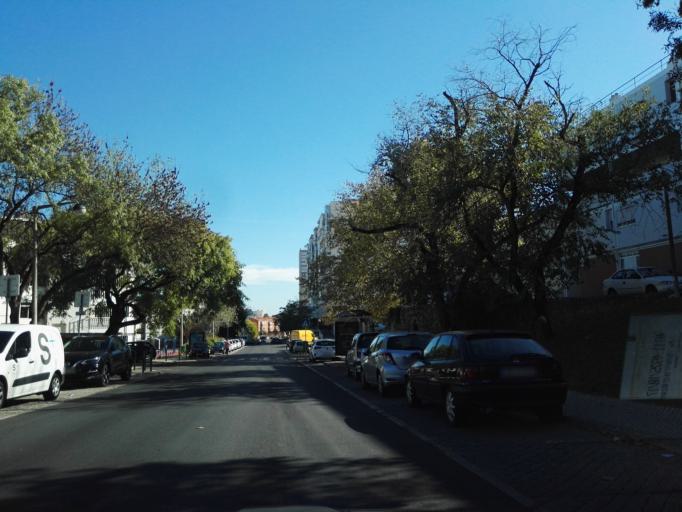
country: PT
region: Lisbon
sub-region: Loures
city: Moscavide
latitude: 38.7763
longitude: -9.1141
